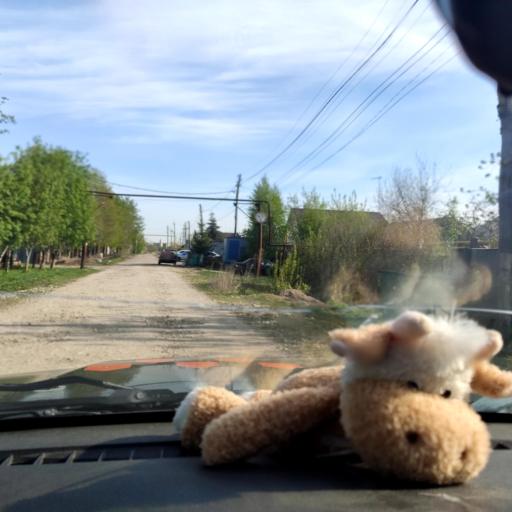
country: RU
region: Samara
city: Tol'yatti
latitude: 53.5719
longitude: 49.3080
